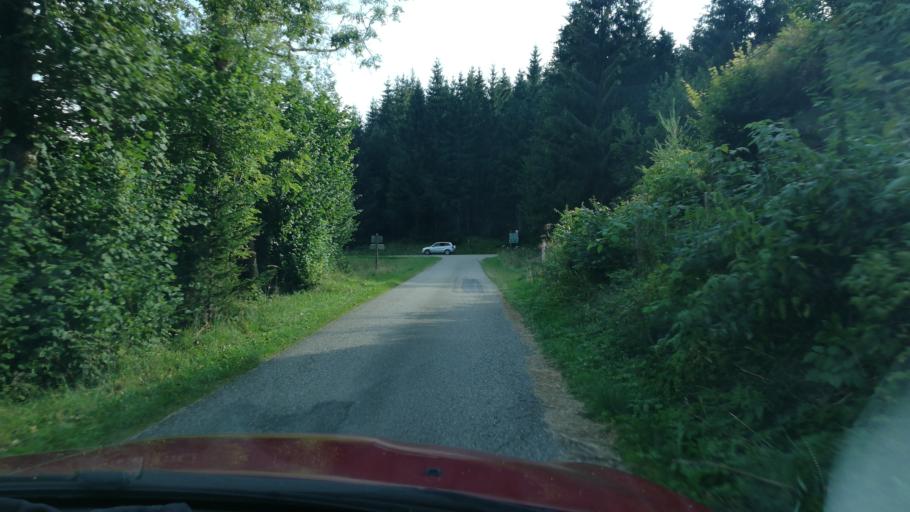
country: AT
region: Lower Austria
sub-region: Politischer Bezirk Zwettl
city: Langschlag
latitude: 48.4748
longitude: 14.8405
